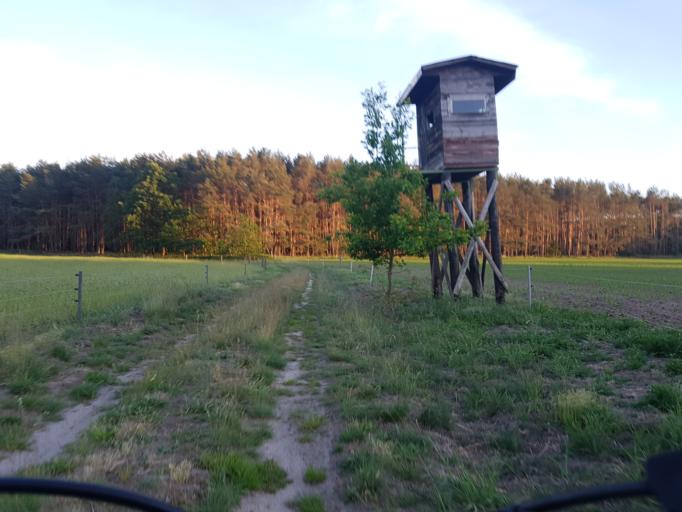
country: DE
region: Brandenburg
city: Bad Liebenwerda
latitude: 51.5557
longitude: 13.3797
